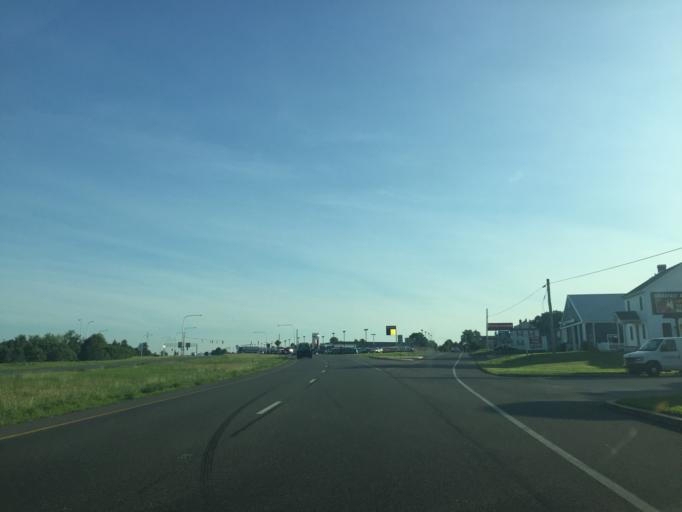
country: US
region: Delaware
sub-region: Kent County
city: Kent Acres
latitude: 39.1389
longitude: -75.5250
